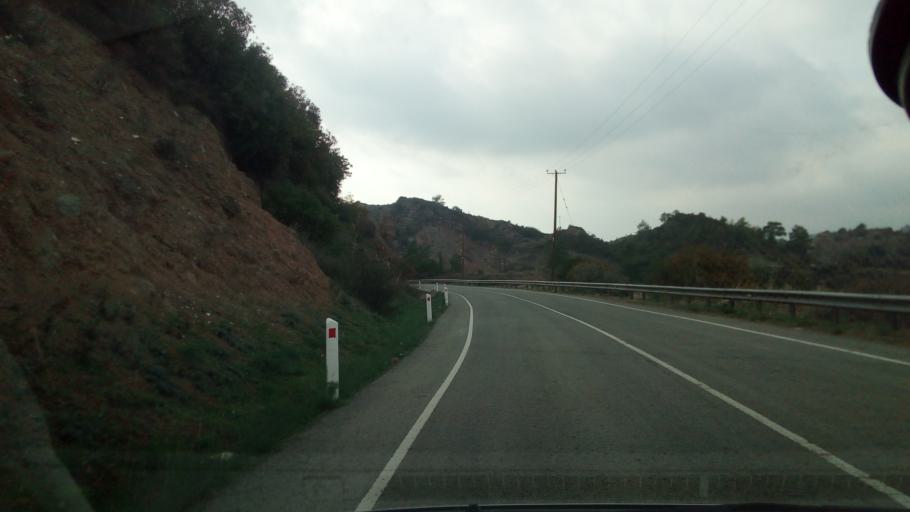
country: CY
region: Lefkosia
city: Lythrodontas
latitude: 34.8702
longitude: 33.2865
